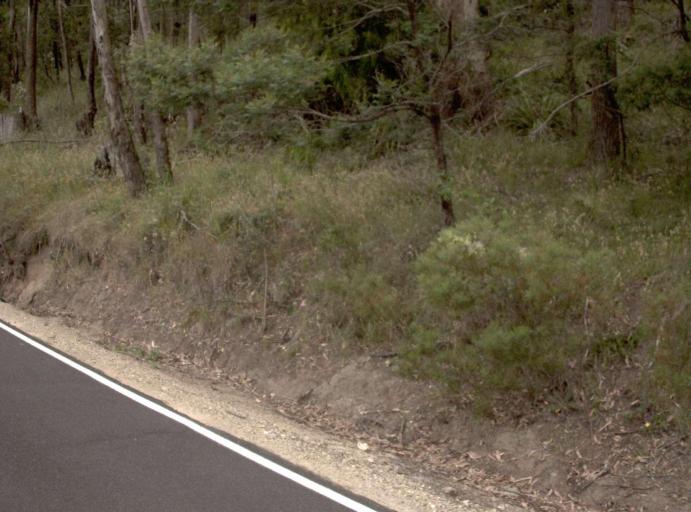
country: AU
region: New South Wales
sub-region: Bombala
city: Bombala
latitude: -37.4491
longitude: 149.1935
